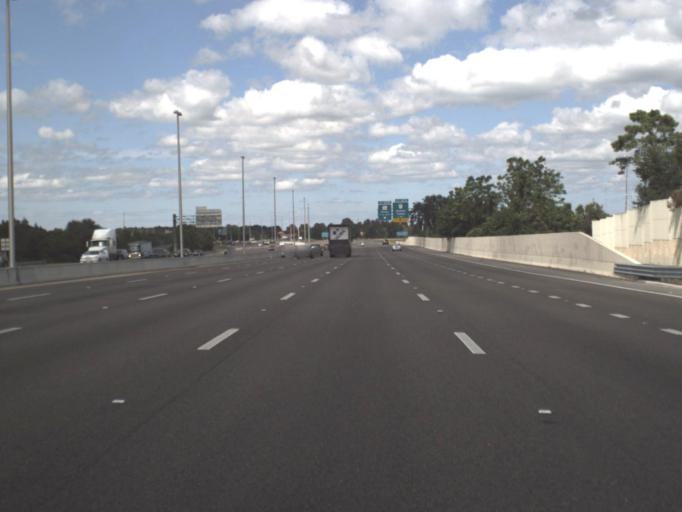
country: US
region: Florida
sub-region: Orange County
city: Gotha
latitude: 28.5391
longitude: -81.5336
